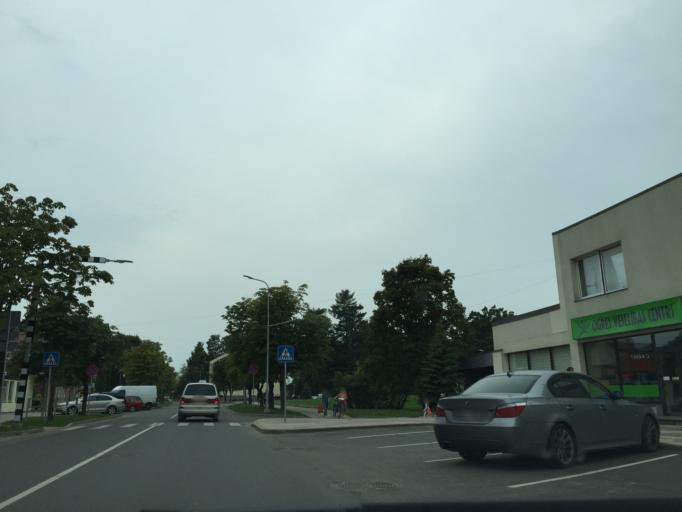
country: LV
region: Ogre
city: Ogre
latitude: 56.8215
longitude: 24.5954
